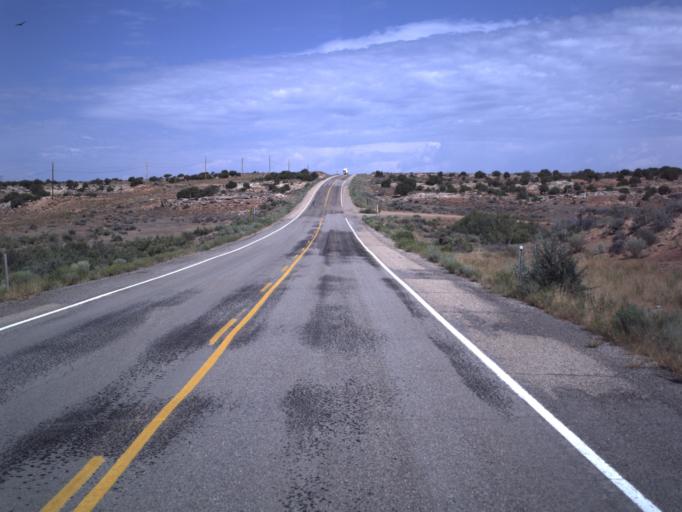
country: US
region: Utah
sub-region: Uintah County
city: Naples
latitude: 40.1647
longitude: -109.3135
